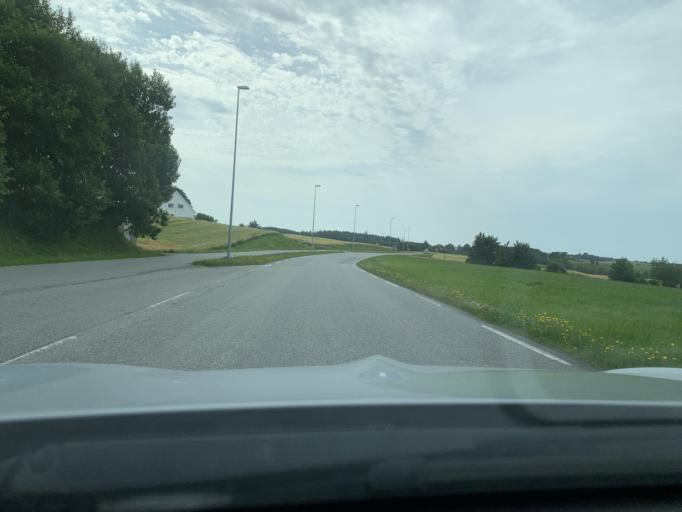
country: NO
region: Rogaland
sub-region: Time
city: Bryne
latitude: 58.7453
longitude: 5.6909
